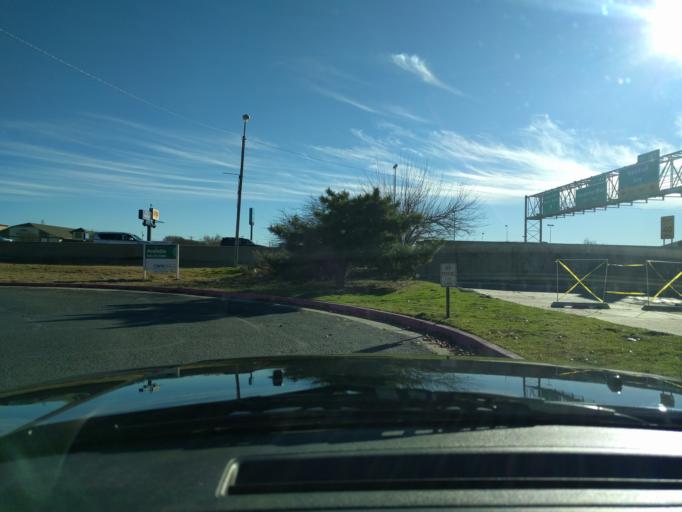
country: US
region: Oklahoma
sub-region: Oklahoma County
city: Warr Acres
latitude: 35.4607
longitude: -97.5971
